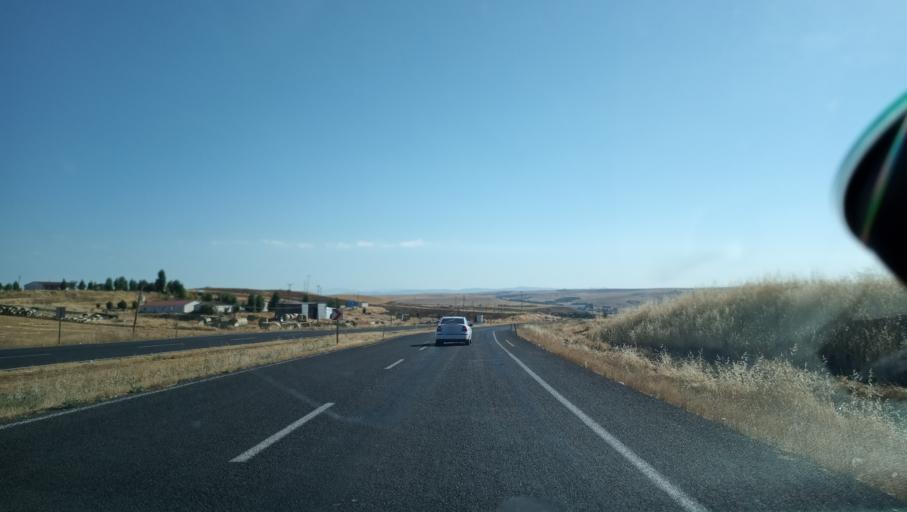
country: TR
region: Diyarbakir
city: Sur
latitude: 37.9841
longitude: 40.3655
